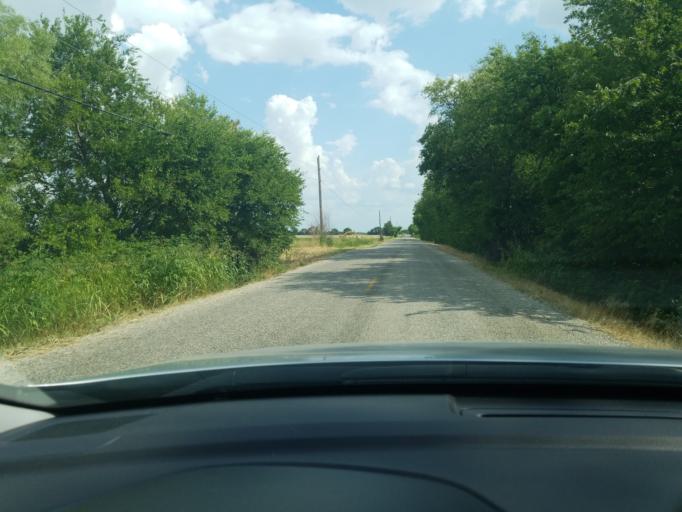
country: US
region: Texas
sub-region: Collin County
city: Prosper
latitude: 33.2864
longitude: -96.8370
